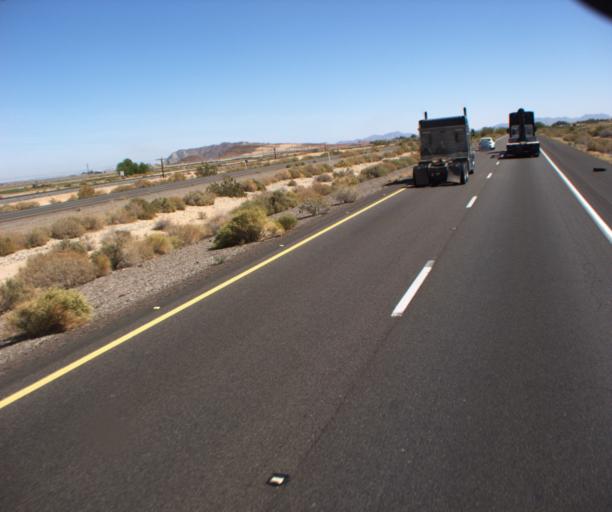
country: US
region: Arizona
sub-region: Yuma County
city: Wellton
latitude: 32.6745
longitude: -114.0707
